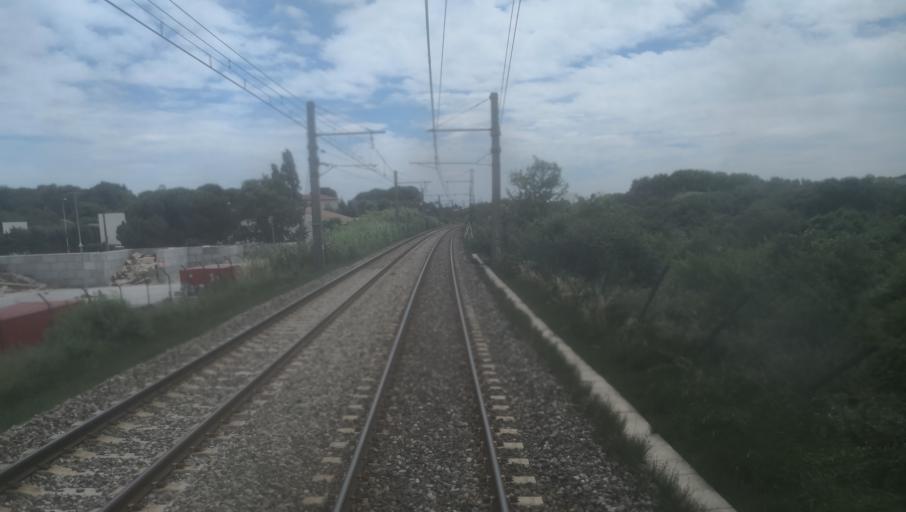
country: FR
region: Languedoc-Roussillon
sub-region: Departement de l'Herault
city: Montpellier
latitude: 43.5835
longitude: 3.8756
